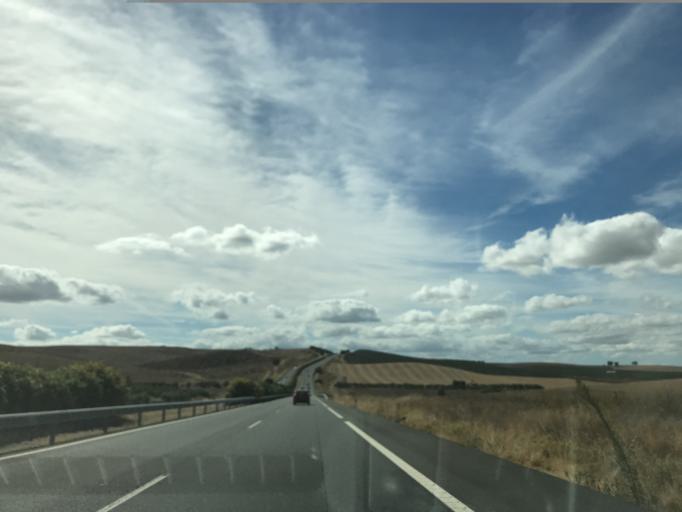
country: ES
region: Andalusia
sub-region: Province of Cordoba
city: La Victoria
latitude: 37.7355
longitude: -4.8516
